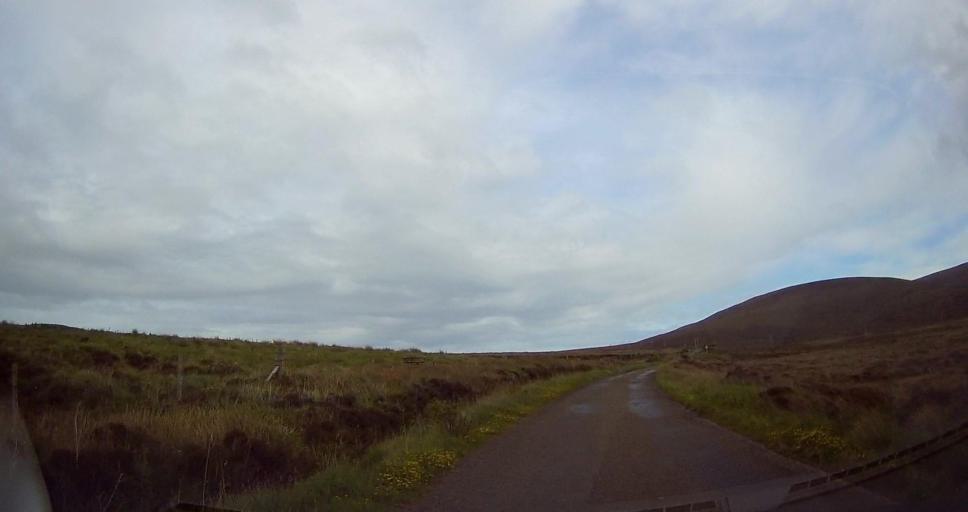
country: GB
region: Scotland
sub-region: Orkney Islands
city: Stromness
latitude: 58.9047
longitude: -3.3097
